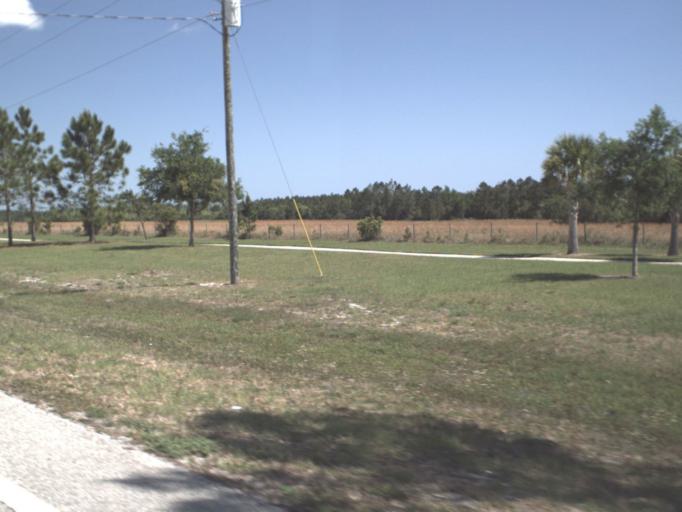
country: US
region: Florida
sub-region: Flagler County
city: Palm Coast
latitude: 29.5648
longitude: -81.2708
